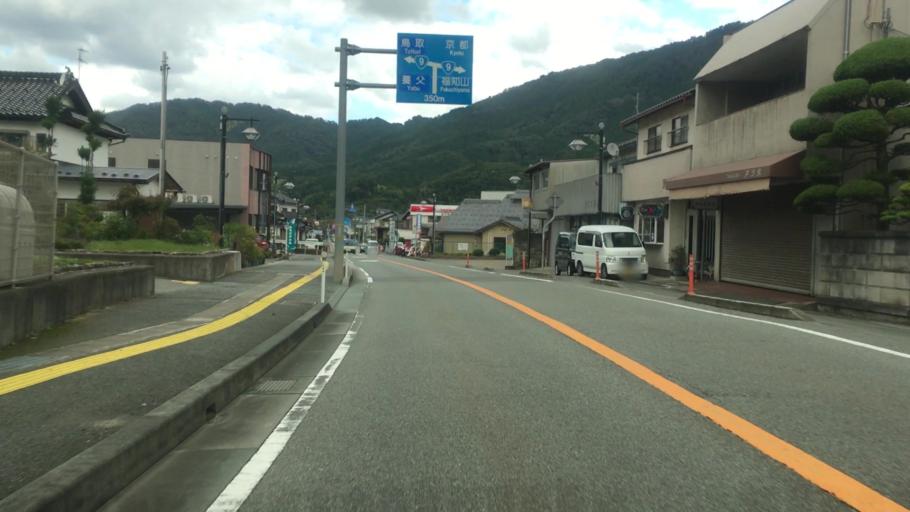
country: JP
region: Hyogo
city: Toyooka
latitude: 35.3155
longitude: 134.8834
